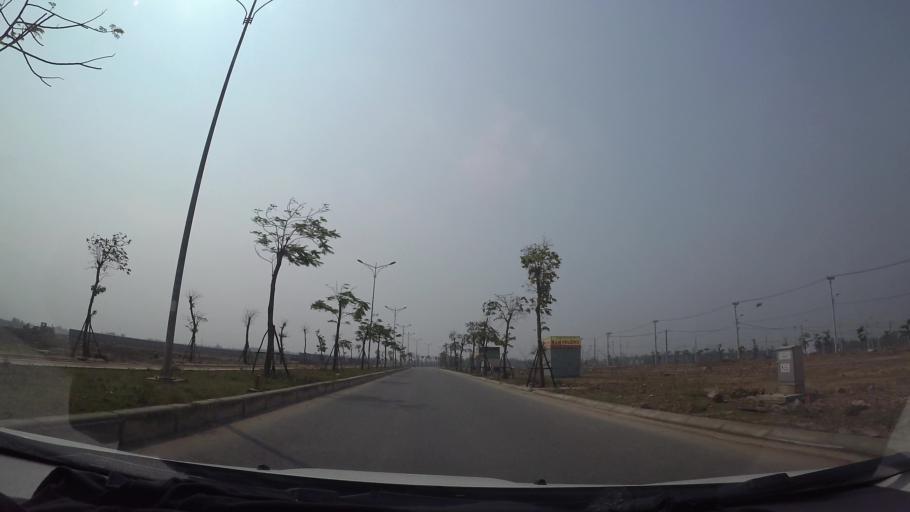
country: VN
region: Da Nang
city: Ngu Hanh Son
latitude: 16.0005
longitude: 108.2473
